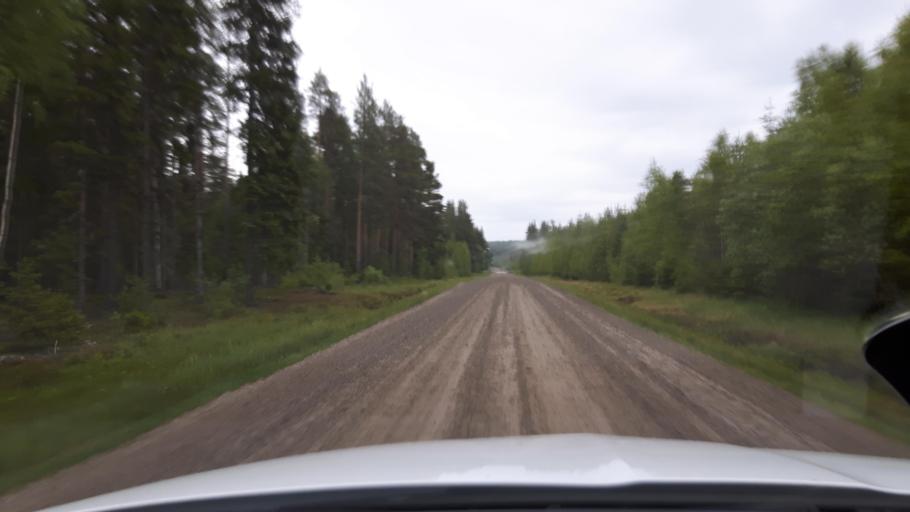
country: SE
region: Gaevleborg
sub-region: Ljusdals Kommun
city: Farila
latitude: 62.1208
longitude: 15.6792
